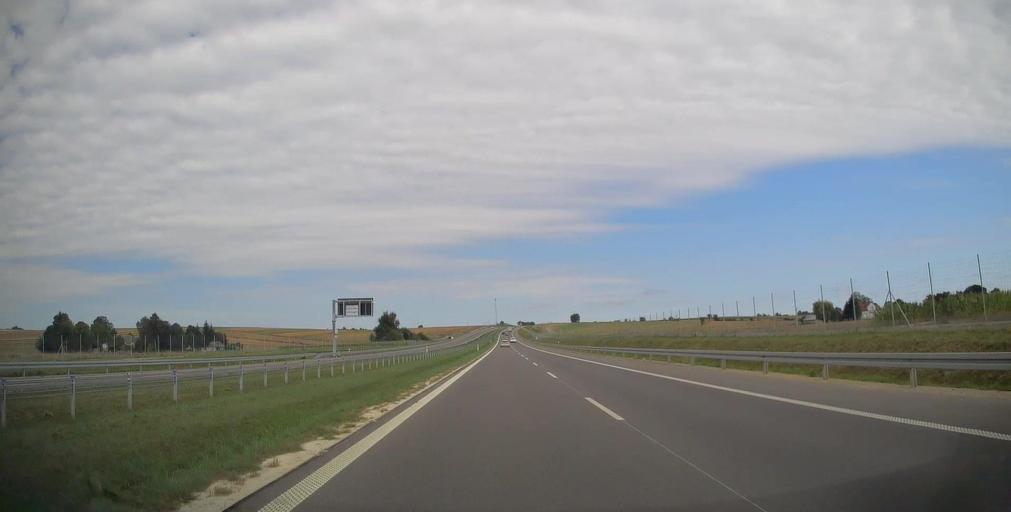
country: PL
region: Lesser Poland Voivodeship
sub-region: Powiat krakowski
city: Slomniki
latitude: 50.2426
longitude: 20.0137
